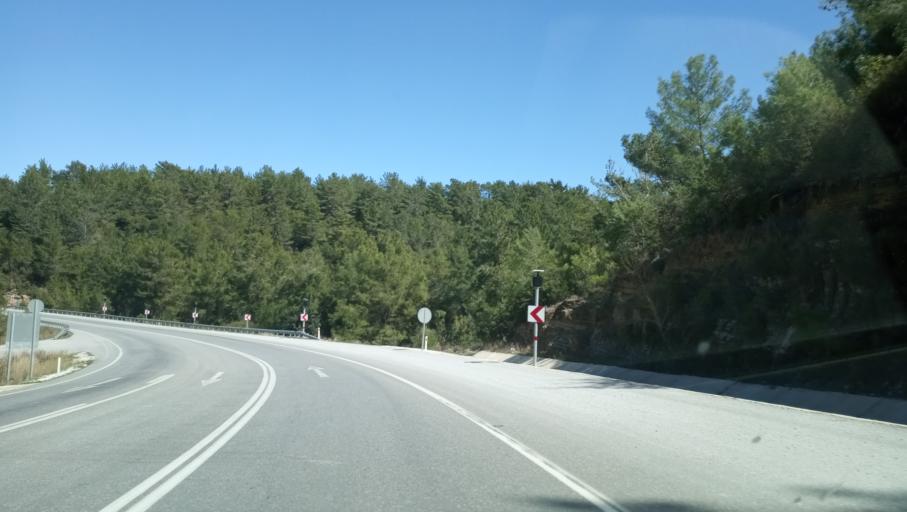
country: TR
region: Antalya
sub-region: Alanya
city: Okurcalar
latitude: 36.7675
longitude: 31.6734
